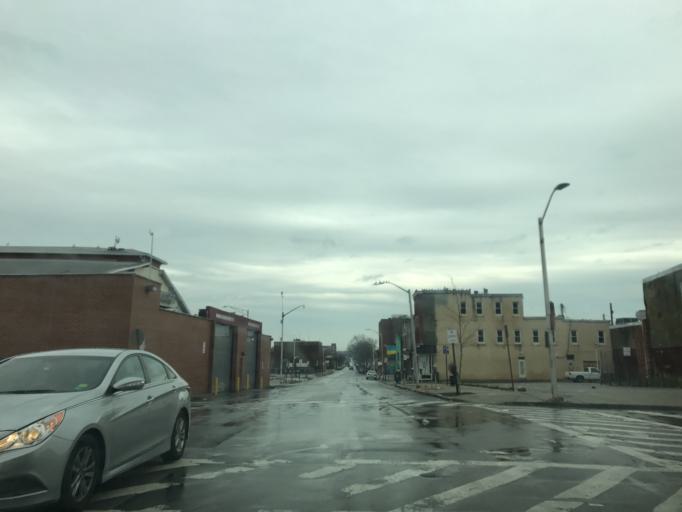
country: US
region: Maryland
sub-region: City of Baltimore
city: Baltimore
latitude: 39.2975
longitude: -76.5880
